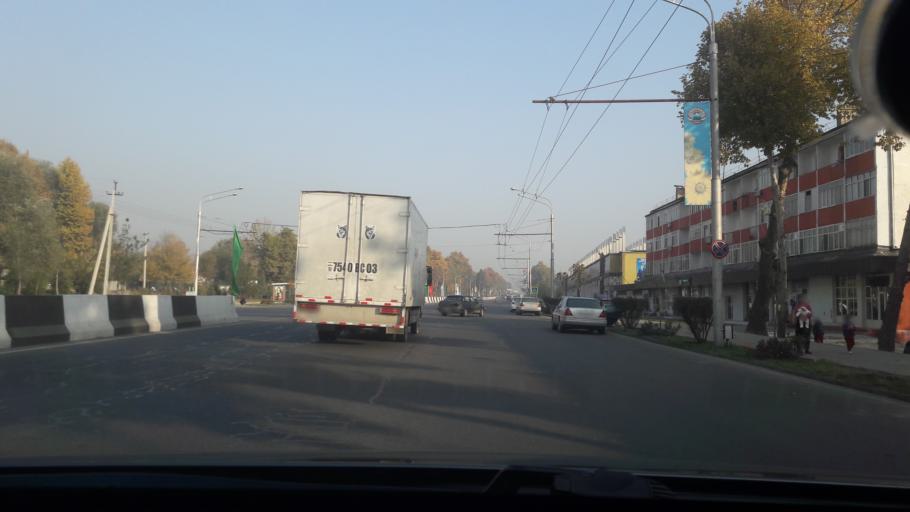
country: TJ
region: Dushanbe
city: Dushanbe
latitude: 38.5532
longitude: 68.8523
